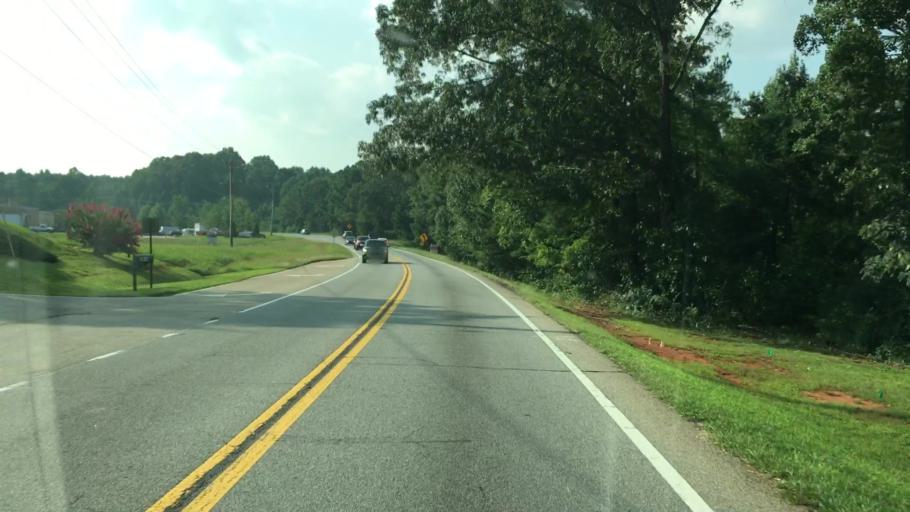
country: US
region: Georgia
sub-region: Jackson County
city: Braselton
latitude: 34.1518
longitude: -83.7999
